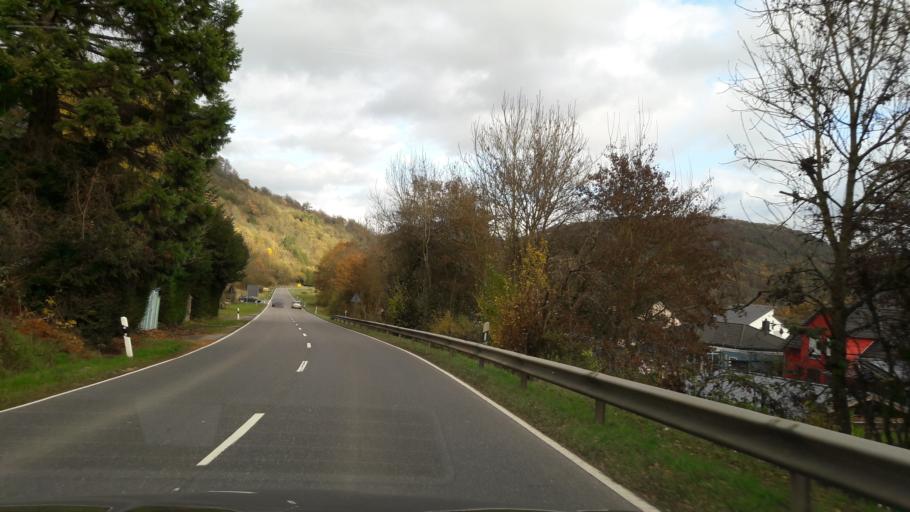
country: LU
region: Grevenmacher
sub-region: Canton d'Echternach
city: Rosport
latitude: 49.8085
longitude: 6.5146
